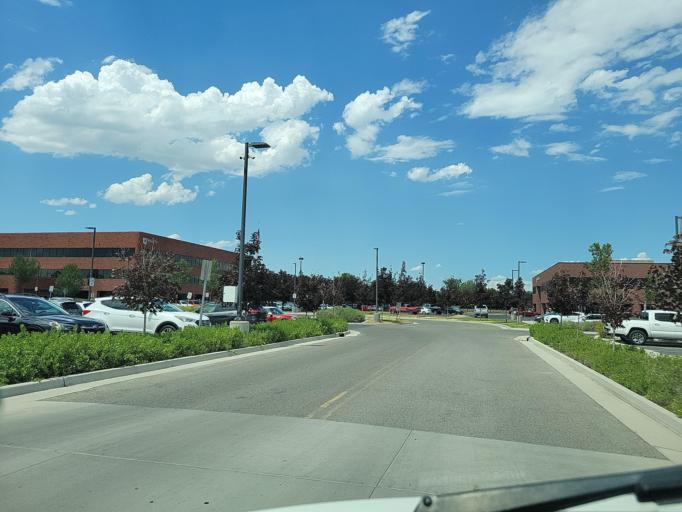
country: US
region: Utah
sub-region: Salt Lake County
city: Murray
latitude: 40.6388
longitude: -111.8845
